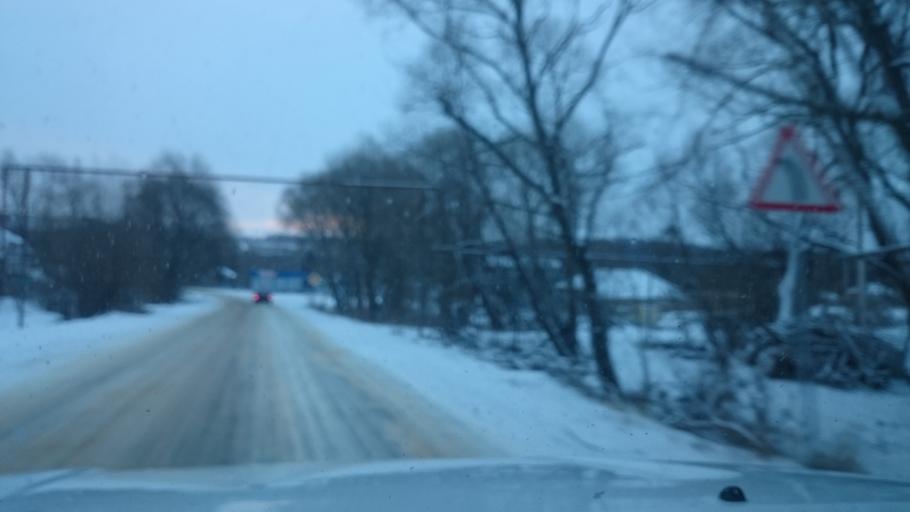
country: RU
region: Tula
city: Leninskiy
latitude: 54.2457
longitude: 37.2594
